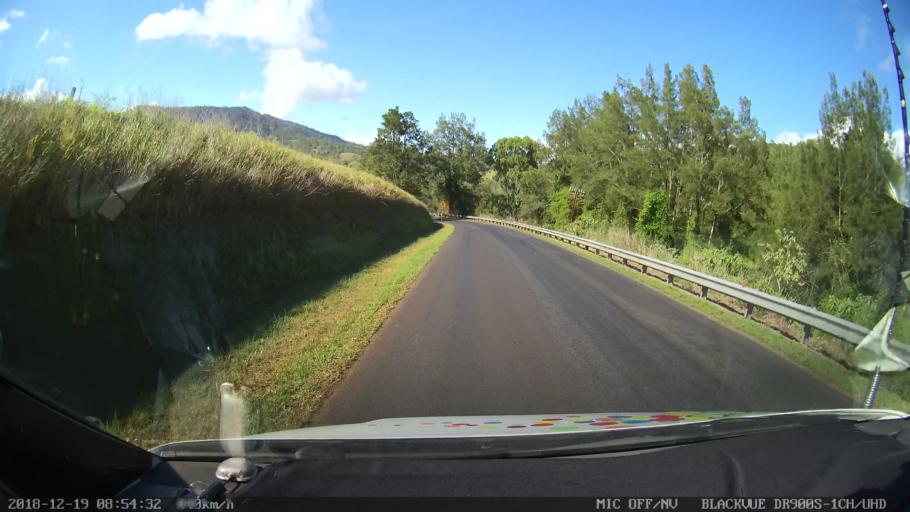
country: AU
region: New South Wales
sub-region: Kyogle
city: Kyogle
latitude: -28.4105
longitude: 152.9782
